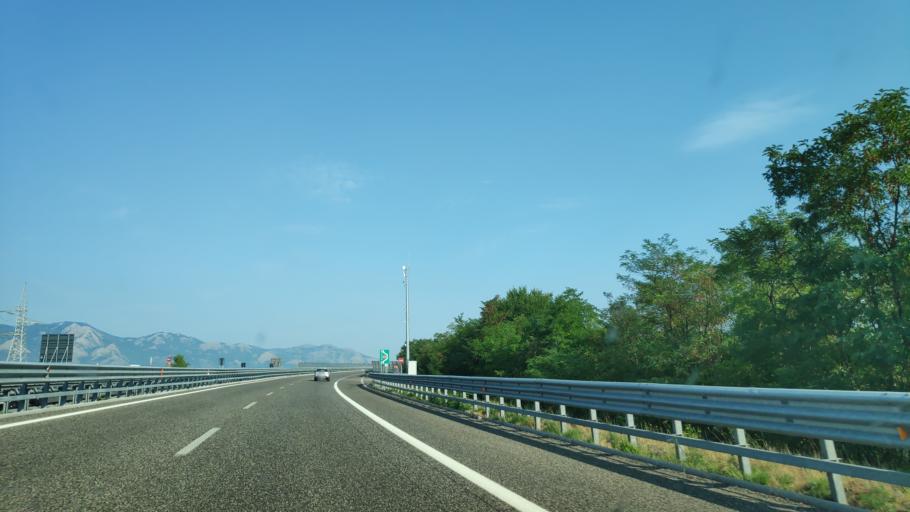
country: IT
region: Campania
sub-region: Provincia di Salerno
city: Sala Consilina
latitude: 40.4102
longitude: 15.5649
